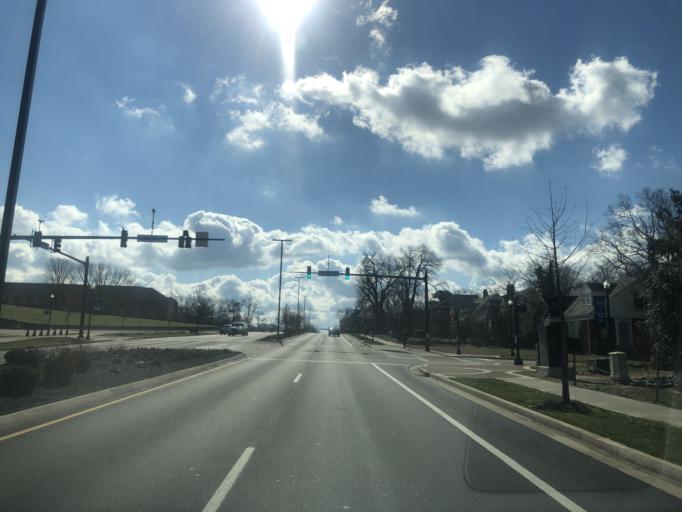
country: US
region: Tennessee
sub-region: Rutherford County
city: Murfreesboro
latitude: 35.8531
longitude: -86.3708
